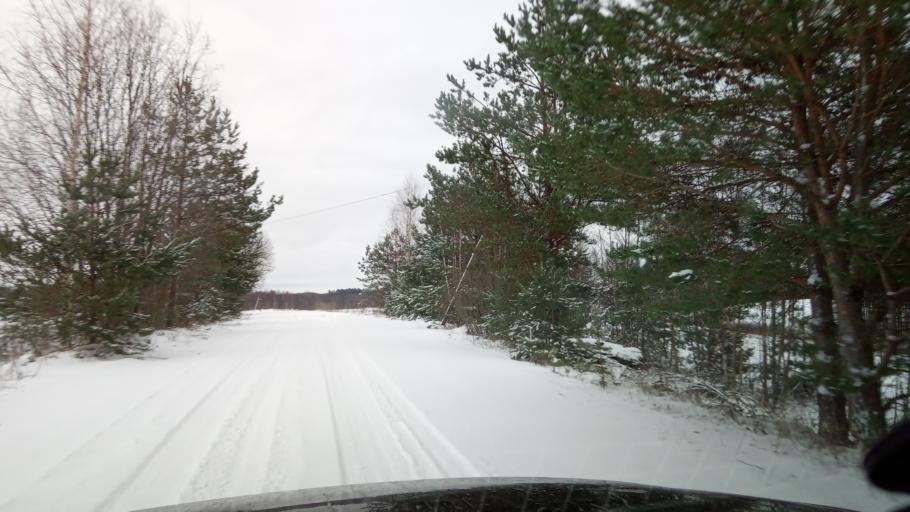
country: LT
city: Zarasai
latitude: 55.6702
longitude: 26.0915
